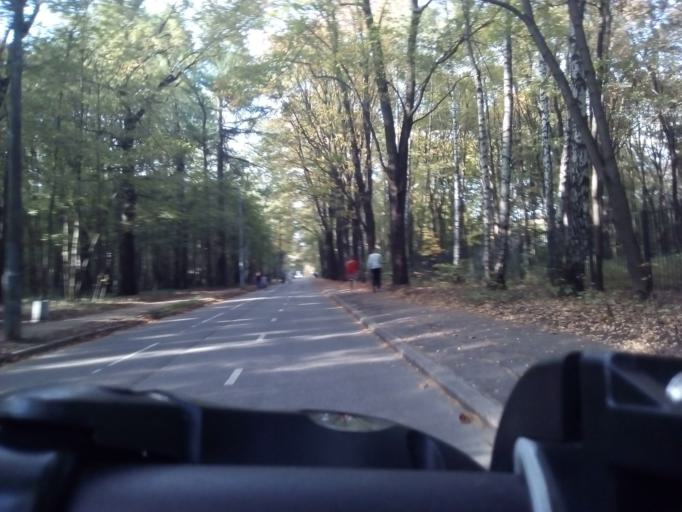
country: RU
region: Moscow
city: Sokol'niki
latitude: 55.8045
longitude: 37.6700
